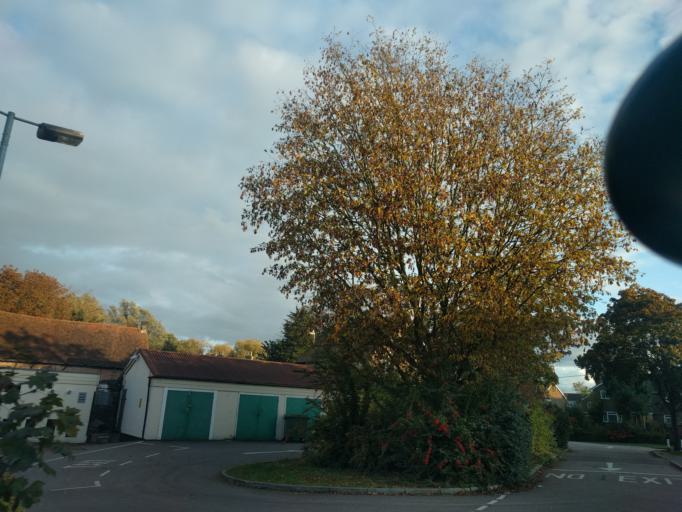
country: GB
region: England
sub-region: Essex
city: Witham
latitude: 51.8081
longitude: 0.6306
